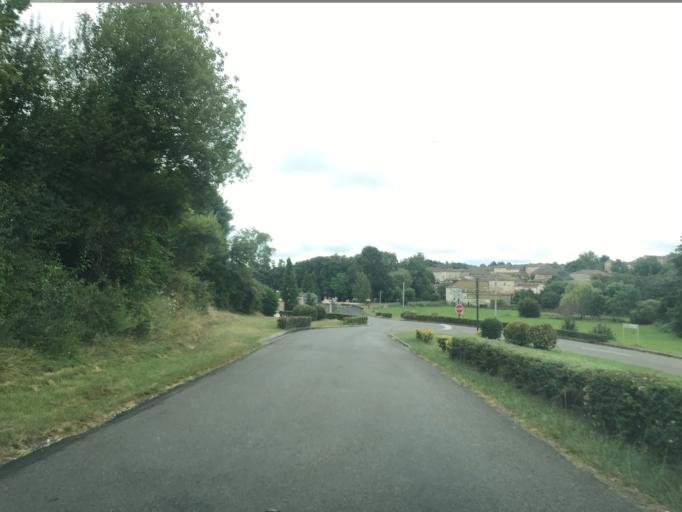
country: FR
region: Poitou-Charentes
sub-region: Departement de la Charente
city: Dirac
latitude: 45.5660
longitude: 0.2116
